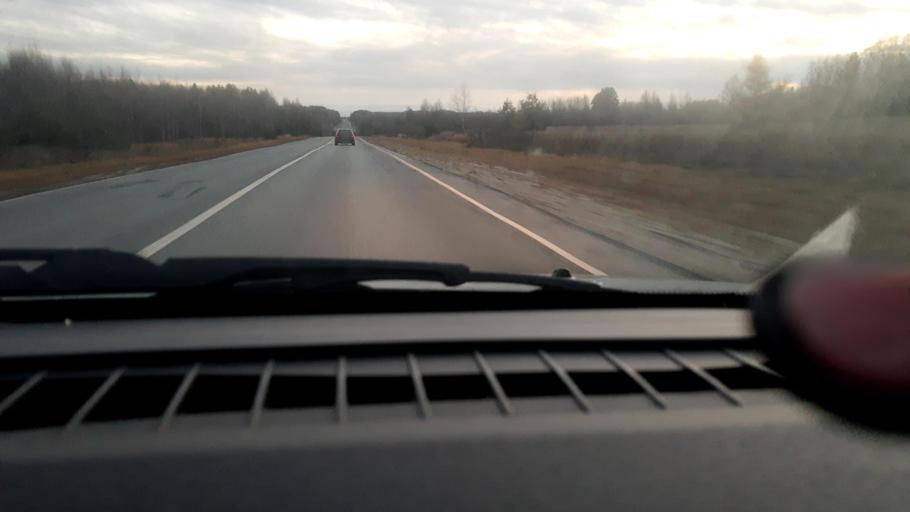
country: RU
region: Nizjnij Novgorod
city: Krasnyye Baki
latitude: 56.9813
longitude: 45.1162
